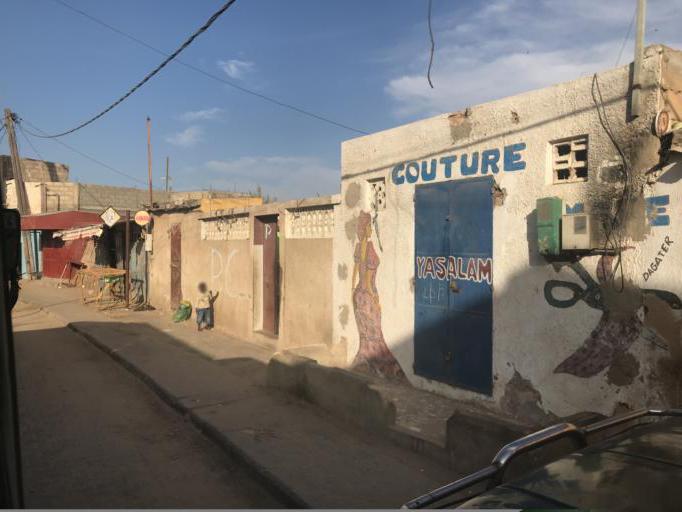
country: SN
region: Saint-Louis
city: Saint-Louis
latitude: 16.0049
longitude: -16.4952
